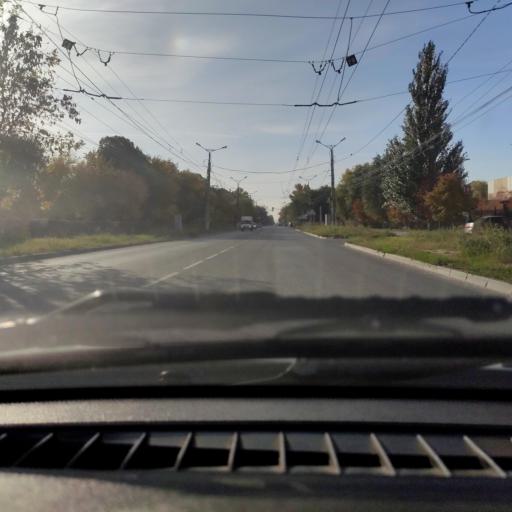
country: RU
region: Samara
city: Tol'yatti
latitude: 53.5212
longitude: 49.4151
